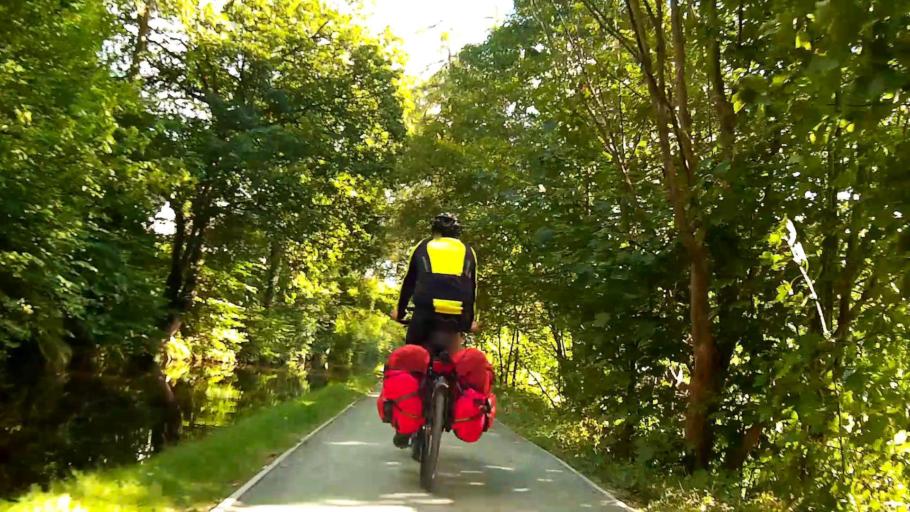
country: GB
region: Wales
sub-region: Denbighshire
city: Llangollen
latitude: 52.9729
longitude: -3.1729
